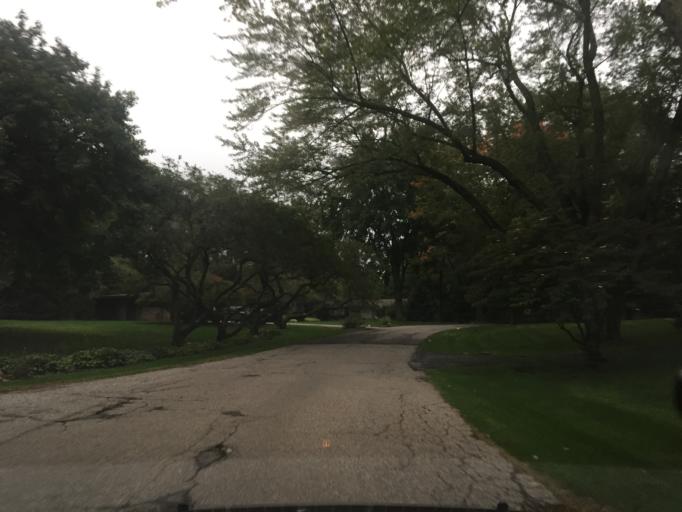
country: US
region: Michigan
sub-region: Oakland County
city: Franklin
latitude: 42.5581
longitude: -83.2875
